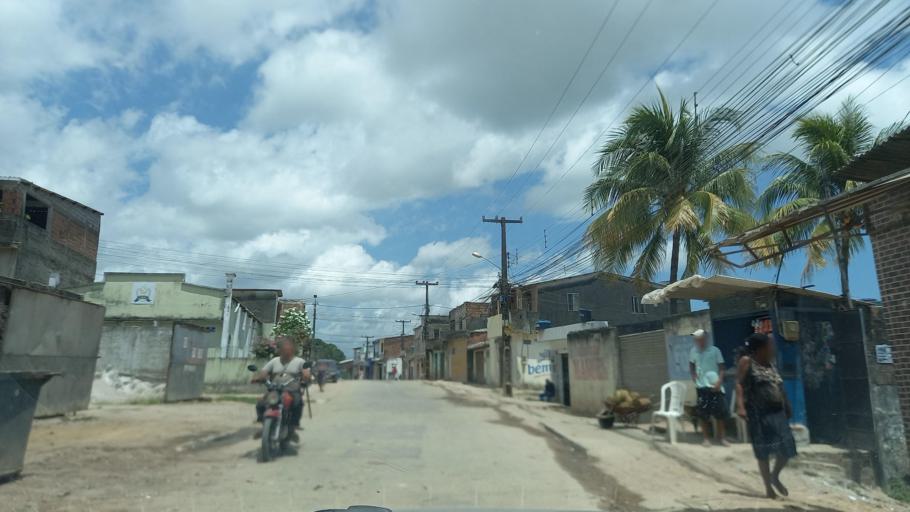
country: BR
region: Pernambuco
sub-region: Jaboatao Dos Guararapes
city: Jaboatao
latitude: -8.1711
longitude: -35.0041
